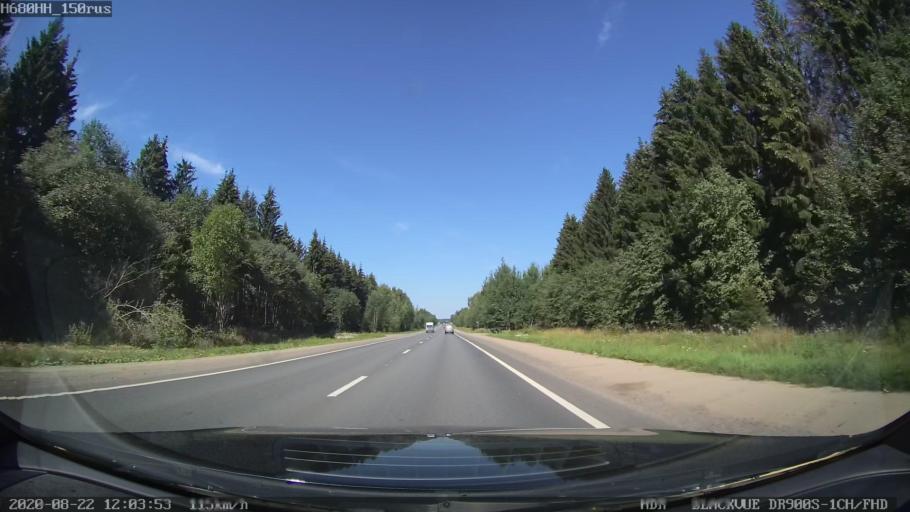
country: RU
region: Tverskaya
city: Rameshki
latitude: 57.2609
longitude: 36.0797
